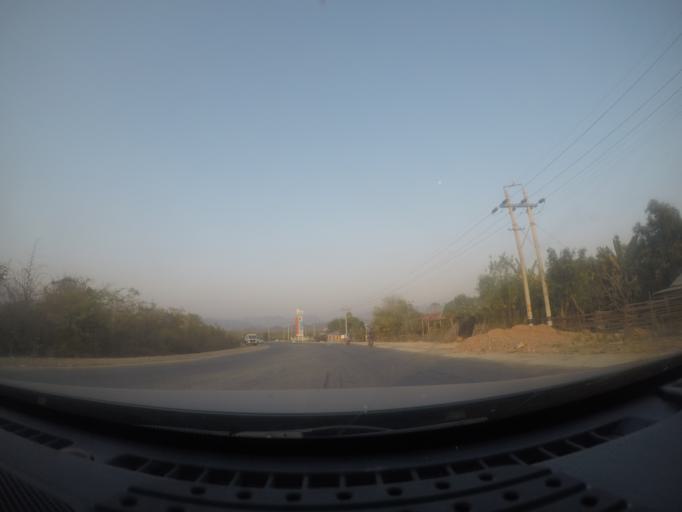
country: MM
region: Mandalay
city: Yamethin
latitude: 20.7771
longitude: 96.3325
